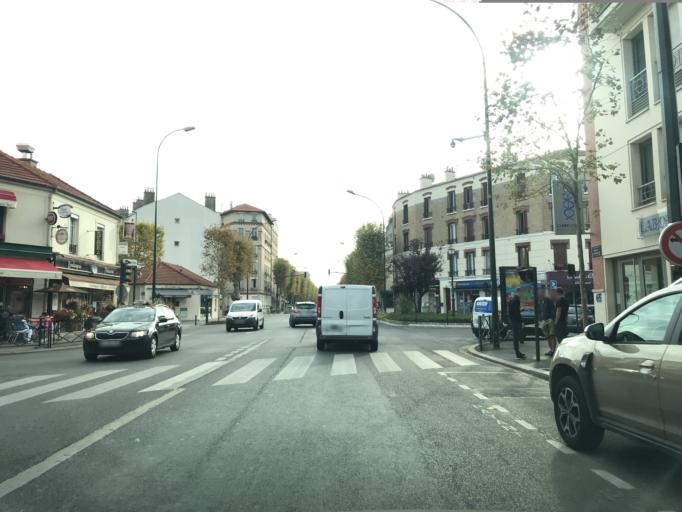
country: FR
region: Ile-de-France
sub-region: Departement des Hauts-de-Seine
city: La Garenne-Colombes
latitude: 48.9070
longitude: 2.2432
